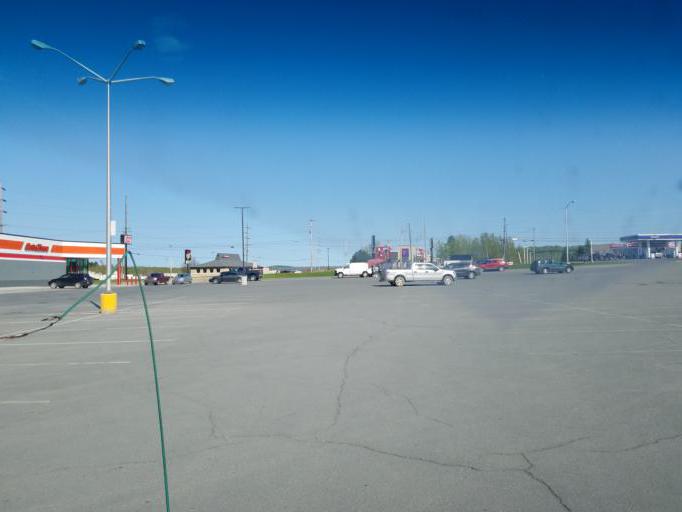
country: US
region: Maine
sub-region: Aroostook County
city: Presque Isle
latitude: 46.7003
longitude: -68.0121
